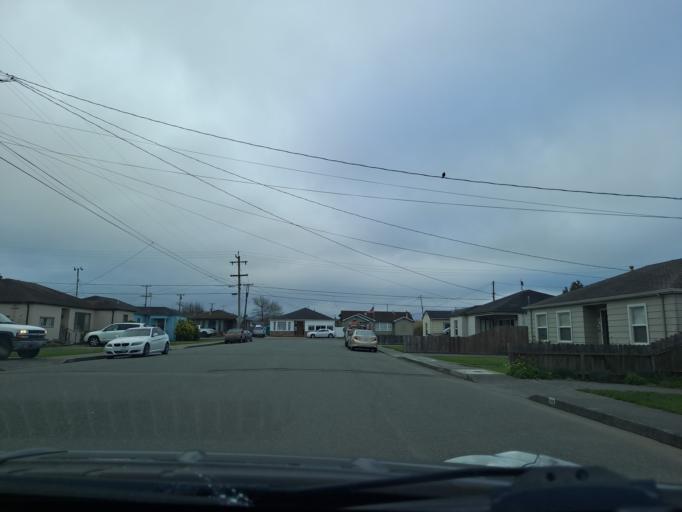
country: US
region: California
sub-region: Humboldt County
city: Fortuna
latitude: 40.5892
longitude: -124.1504
